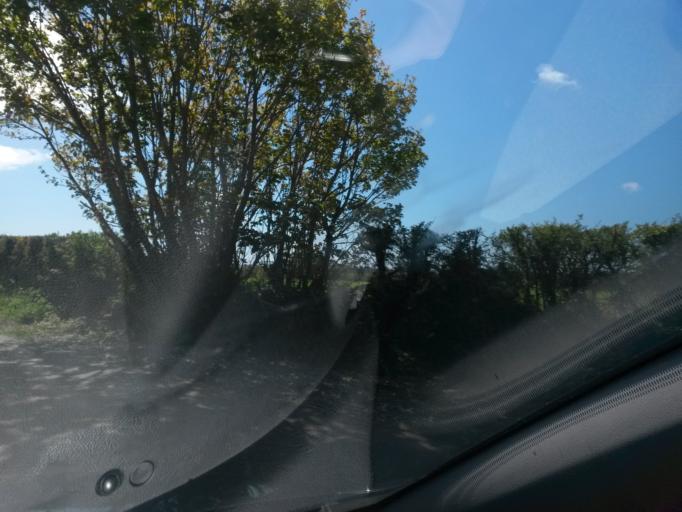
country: IE
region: Munster
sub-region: Waterford
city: Dunmore East
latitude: 52.2405
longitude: -6.8567
